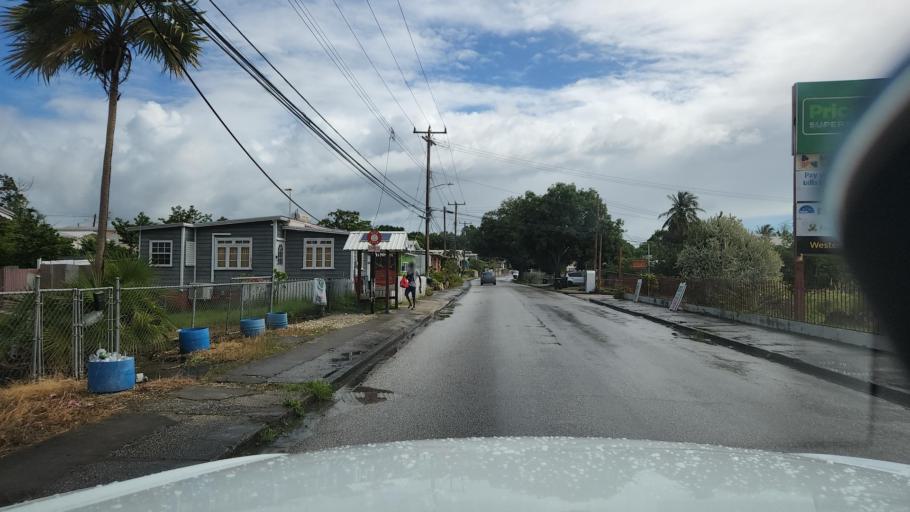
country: BB
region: Christ Church
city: Oistins
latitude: 13.0867
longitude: -59.5732
